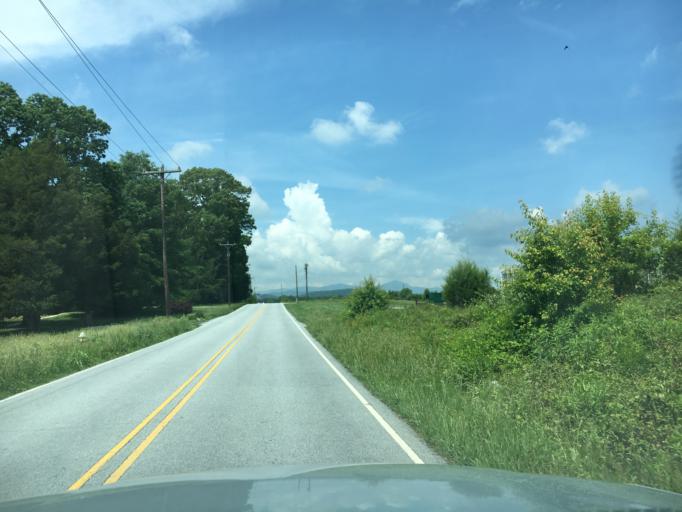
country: US
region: North Carolina
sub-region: Henderson County
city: Mills River
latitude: 35.3773
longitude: -82.5491
